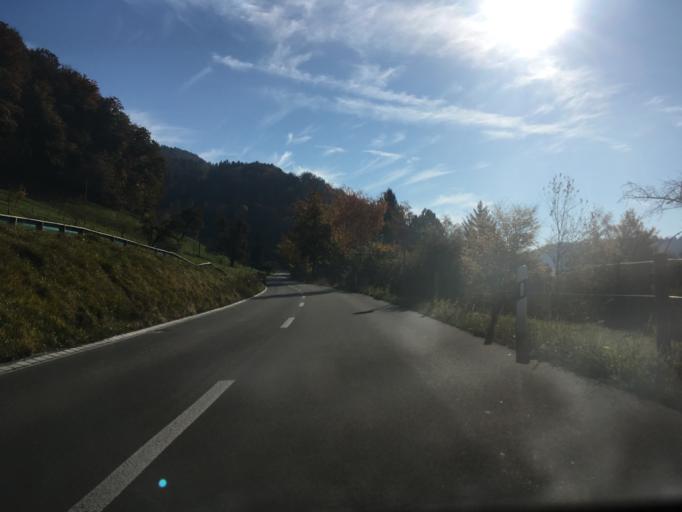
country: CH
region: Zurich
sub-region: Bezirk Horgen
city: Muehlehalde
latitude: 47.2690
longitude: 8.5085
